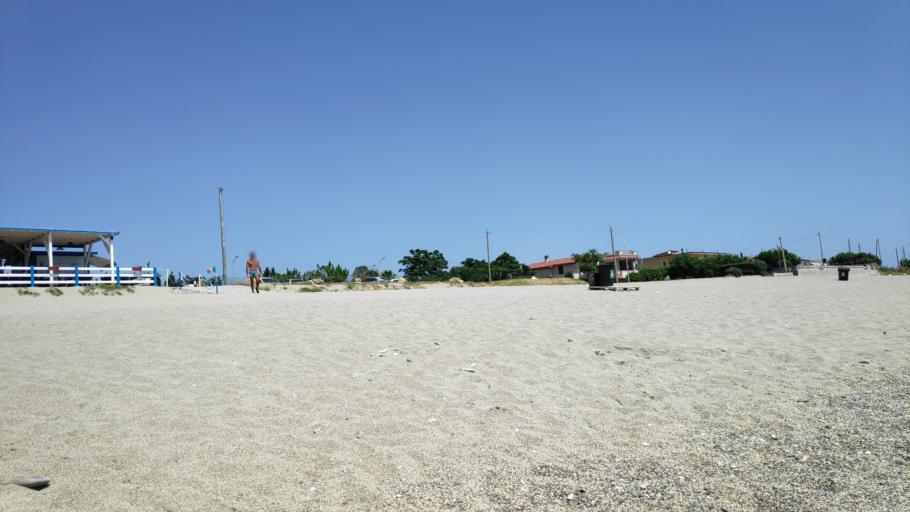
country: IT
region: Calabria
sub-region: Provincia di Reggio Calabria
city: Monasterace Marina
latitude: 38.4148
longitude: 16.5595
